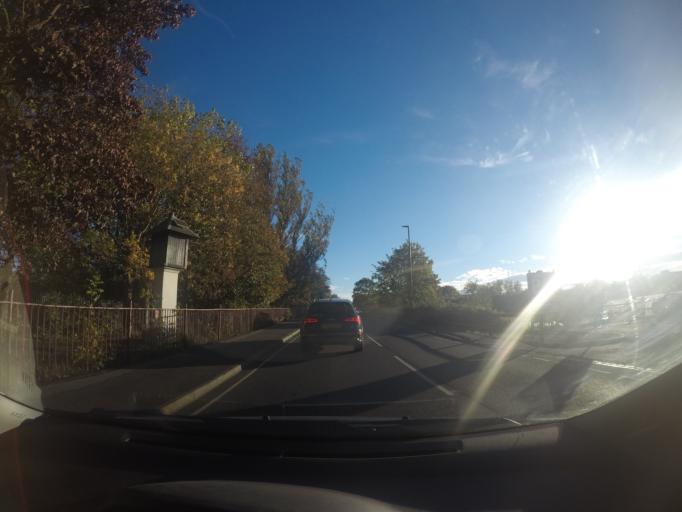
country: GB
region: England
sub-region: City of York
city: York
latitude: 53.9744
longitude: -1.0820
